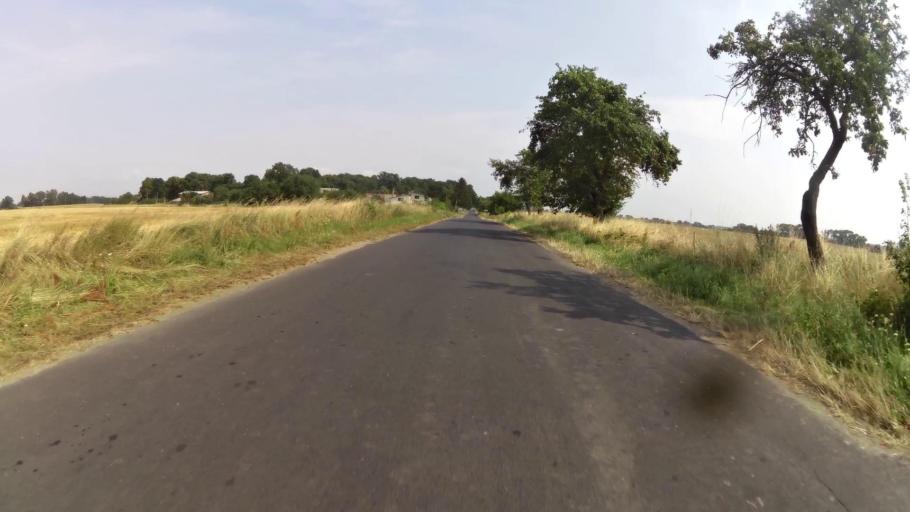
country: PL
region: West Pomeranian Voivodeship
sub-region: Powiat pyrzycki
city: Lipiany
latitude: 52.9708
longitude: 14.9837
